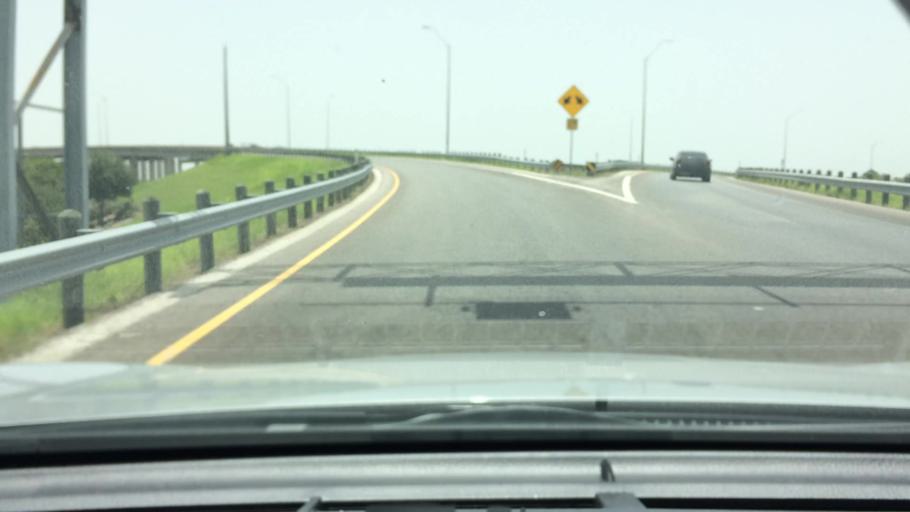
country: US
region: Texas
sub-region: Bexar County
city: China Grove
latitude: 29.3308
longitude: -98.4175
